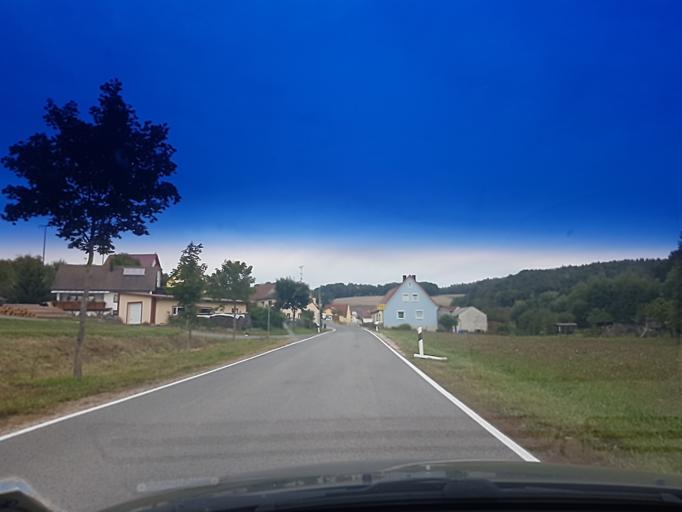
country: DE
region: Bavaria
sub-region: Upper Franconia
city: Burgwindheim
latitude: 49.8353
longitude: 10.5827
